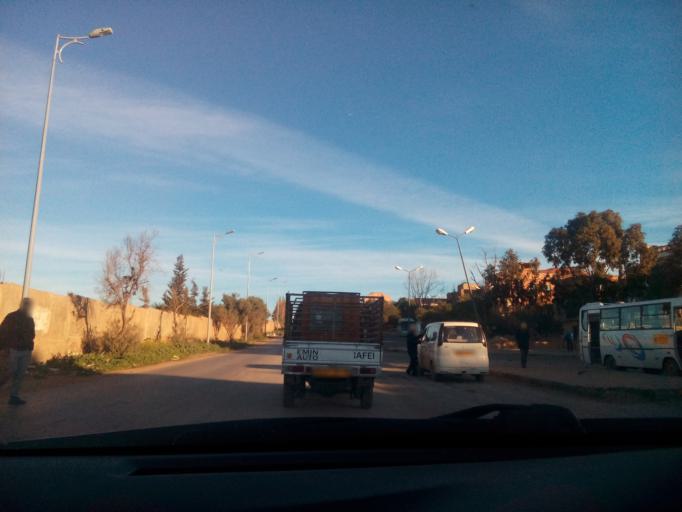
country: DZ
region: Oran
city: Es Senia
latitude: 35.6328
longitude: -0.6741
